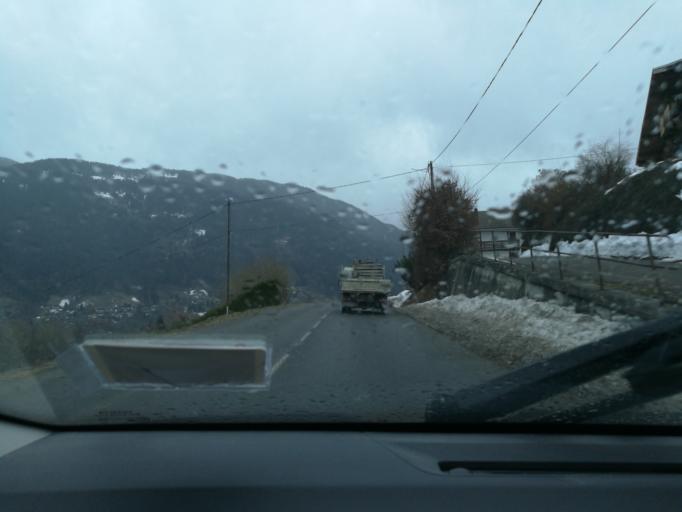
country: FR
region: Rhone-Alpes
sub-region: Departement de la Haute-Savoie
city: Saint-Gervais-les-Bains
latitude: 45.8935
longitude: 6.6997
